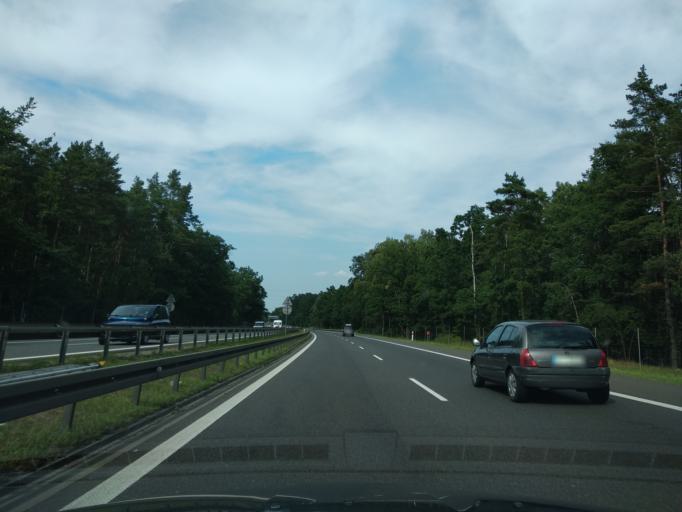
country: PL
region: West Pomeranian Voivodeship
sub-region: Powiat gryfinski
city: Stare Czarnowo
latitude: 53.3817
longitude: 14.7106
